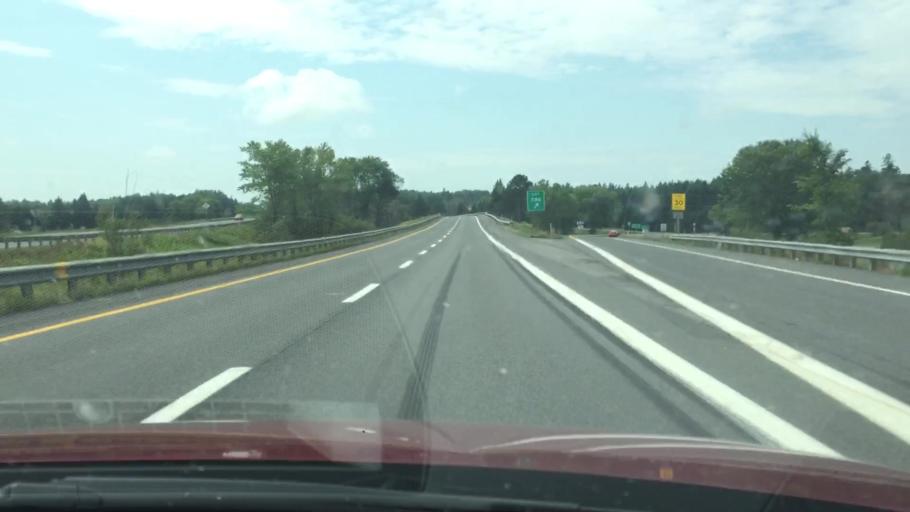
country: US
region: Maine
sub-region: Aroostook County
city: Hodgdon
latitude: 46.1113
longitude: -68.1573
